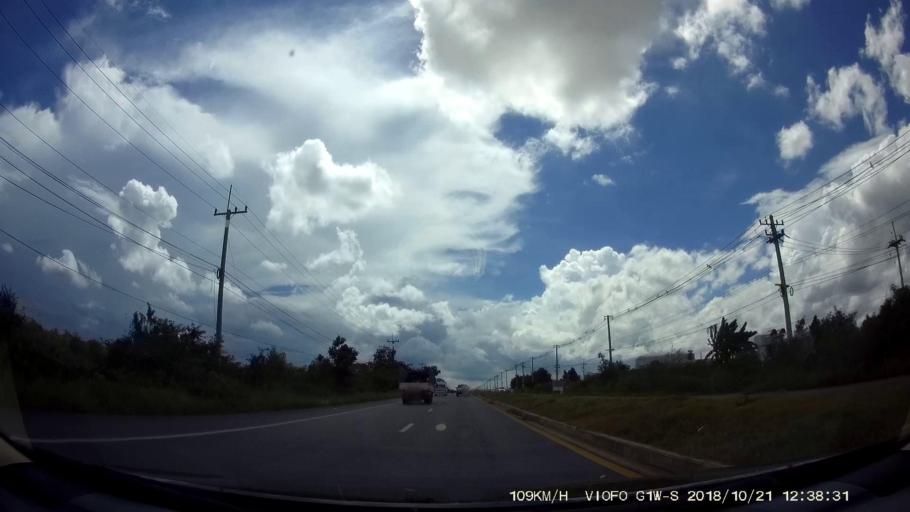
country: TH
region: Nakhon Ratchasima
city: Amphoe Sikhiu
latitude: 15.0527
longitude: 101.7056
